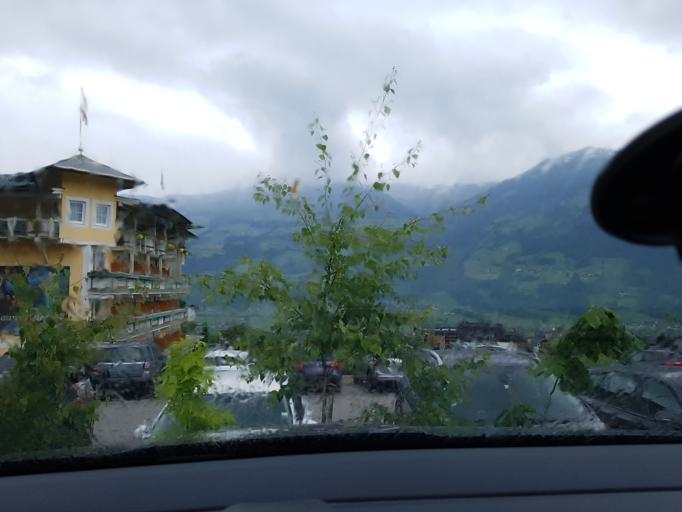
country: AT
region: Tyrol
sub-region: Politischer Bezirk Schwaz
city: Fugen
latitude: 47.3393
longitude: 11.8438
